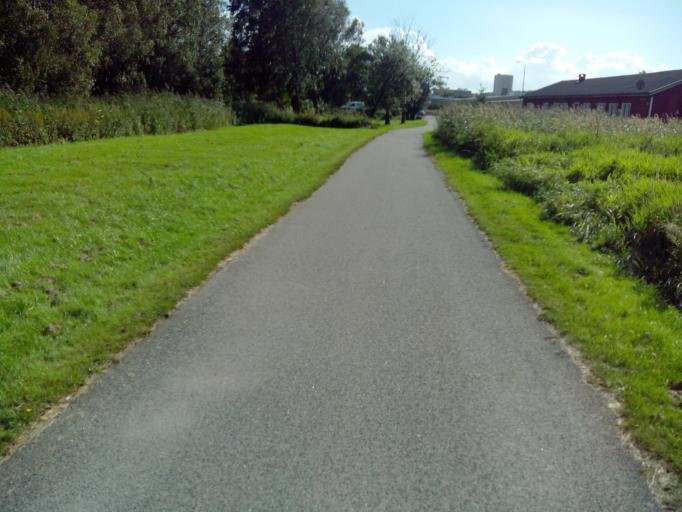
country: SE
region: Vaestra Goetaland
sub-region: Goteborg
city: Goeteborg
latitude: 57.7307
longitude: 11.9524
